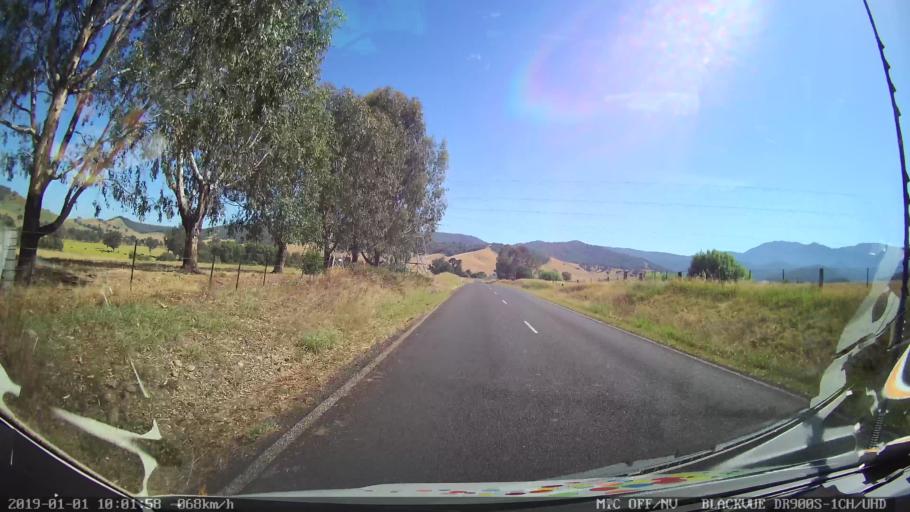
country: AU
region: New South Wales
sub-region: Snowy River
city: Jindabyne
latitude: -36.1860
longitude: 148.1012
